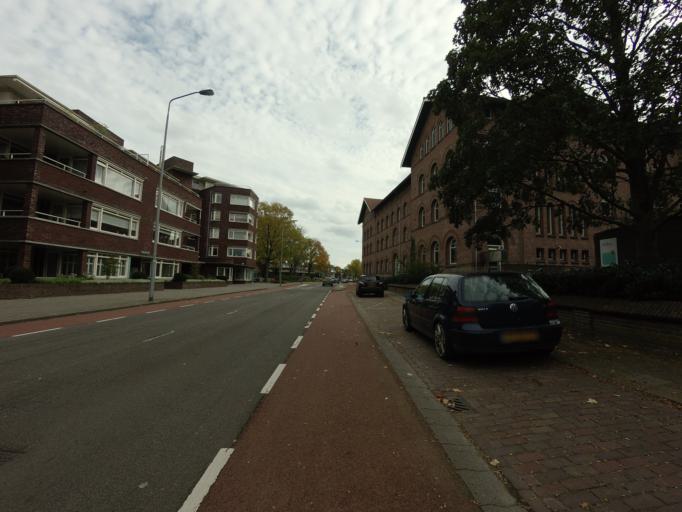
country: NL
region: North Brabant
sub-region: Gemeente Breda
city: Breda
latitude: 51.5791
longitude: 4.7893
